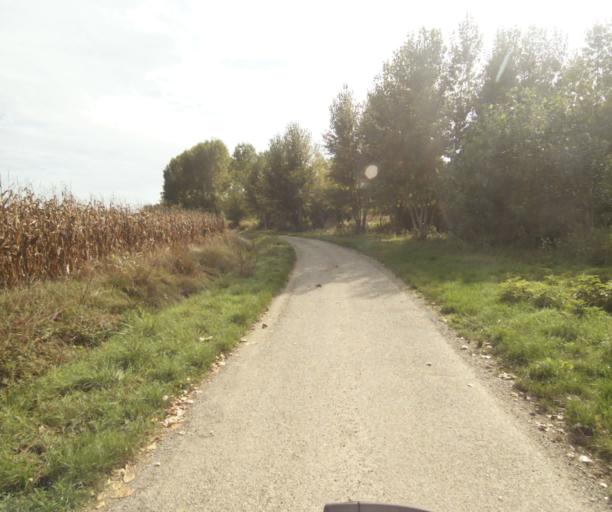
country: FR
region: Midi-Pyrenees
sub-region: Departement du Tarn-et-Garonne
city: Finhan
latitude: 43.9135
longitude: 1.1969
